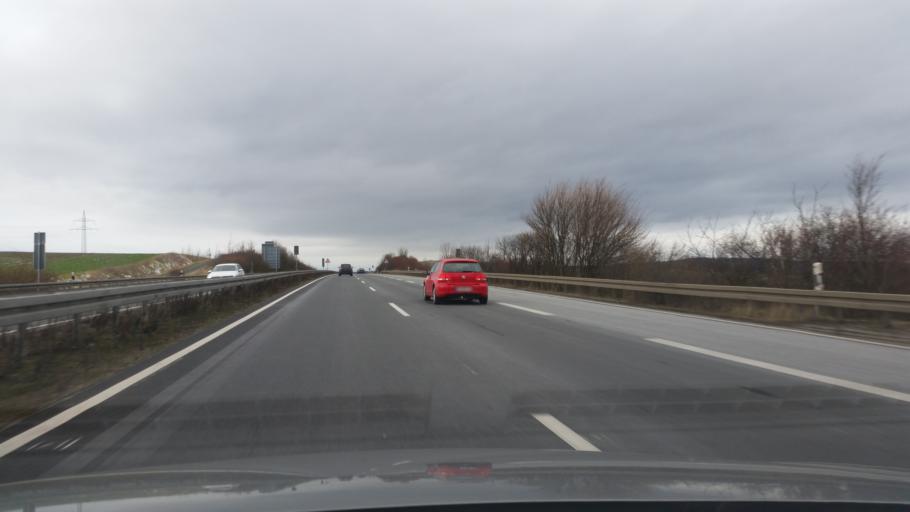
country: DE
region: Lower Saxony
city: Schladen
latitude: 52.0284
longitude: 10.5206
